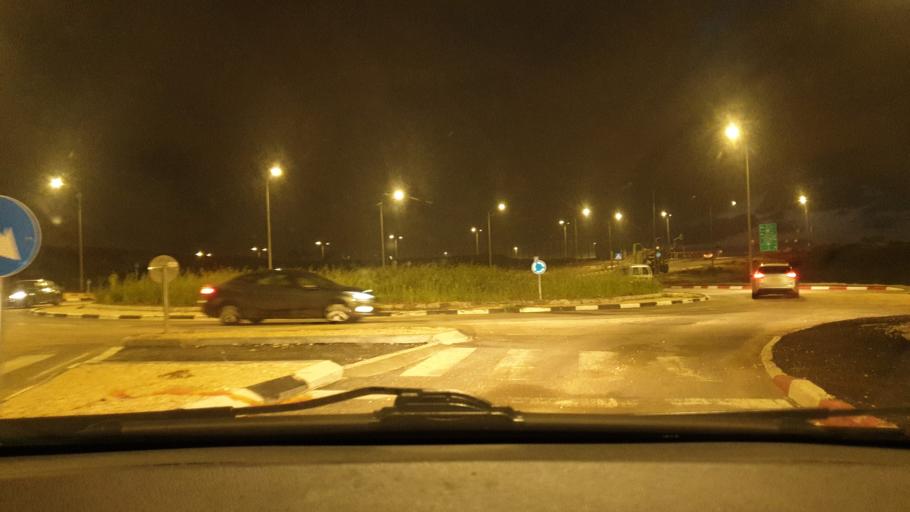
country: IL
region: Central District
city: Ramla
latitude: 31.9368
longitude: 34.8550
